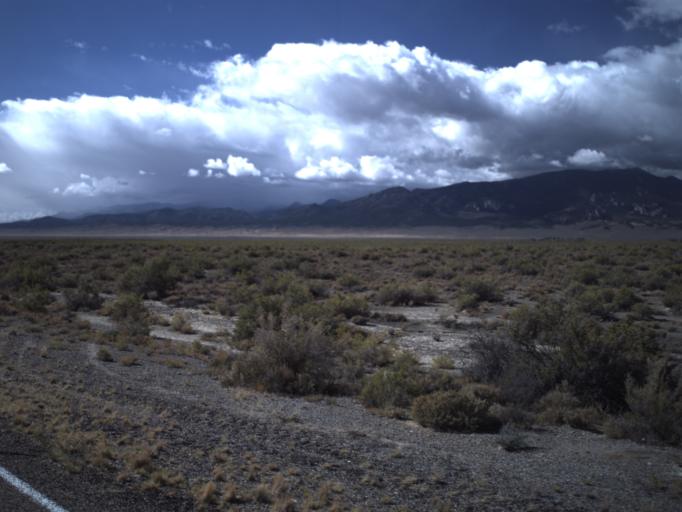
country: US
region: Nevada
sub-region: White Pine County
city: McGill
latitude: 39.0537
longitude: -114.0365
